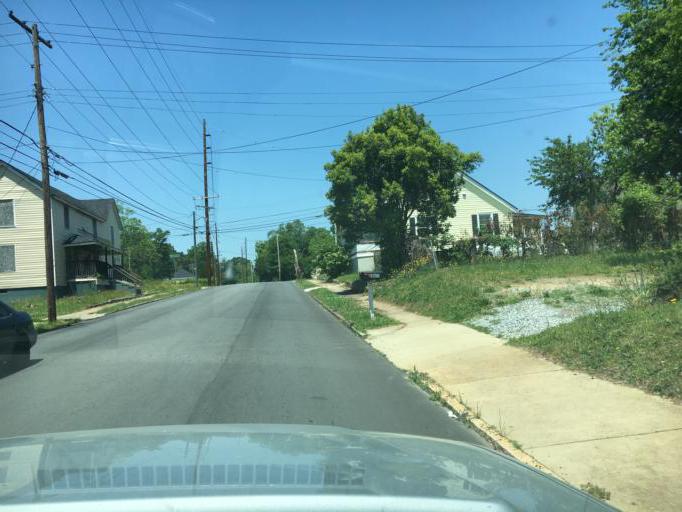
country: US
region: South Carolina
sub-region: Spartanburg County
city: Spartanburg
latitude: 34.9527
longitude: -81.9441
